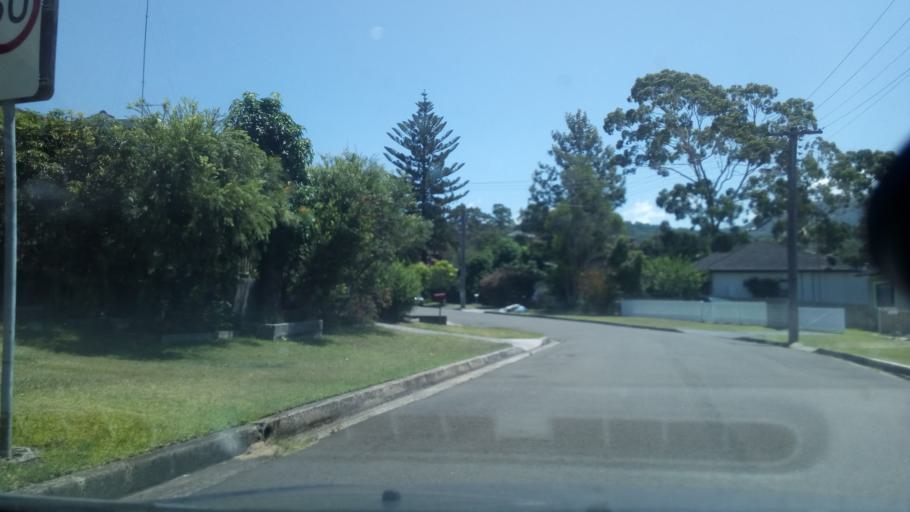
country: AU
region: New South Wales
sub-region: Wollongong
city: West Wollongong
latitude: -34.4281
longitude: 150.8584
